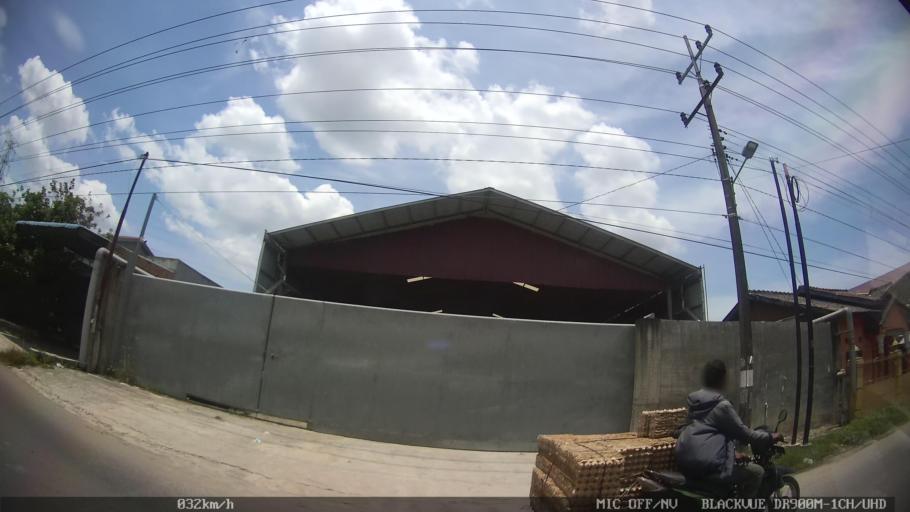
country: ID
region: North Sumatra
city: Binjai
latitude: 3.6244
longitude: 98.5183
